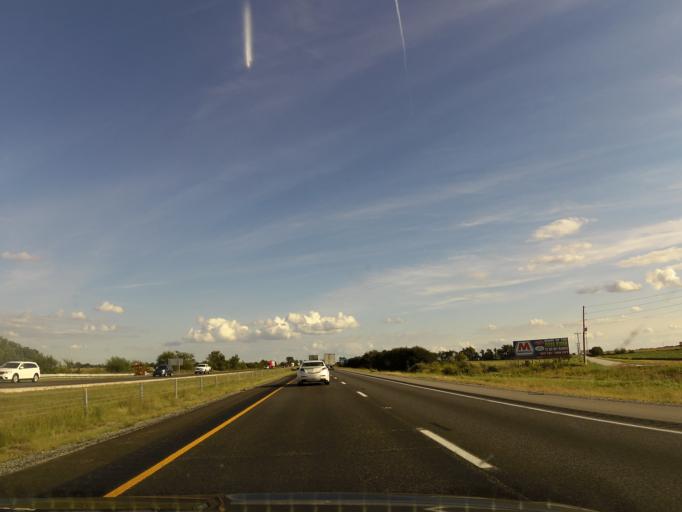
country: US
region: Indiana
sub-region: Jasper County
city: Remington
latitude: 40.7925
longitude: -87.1376
